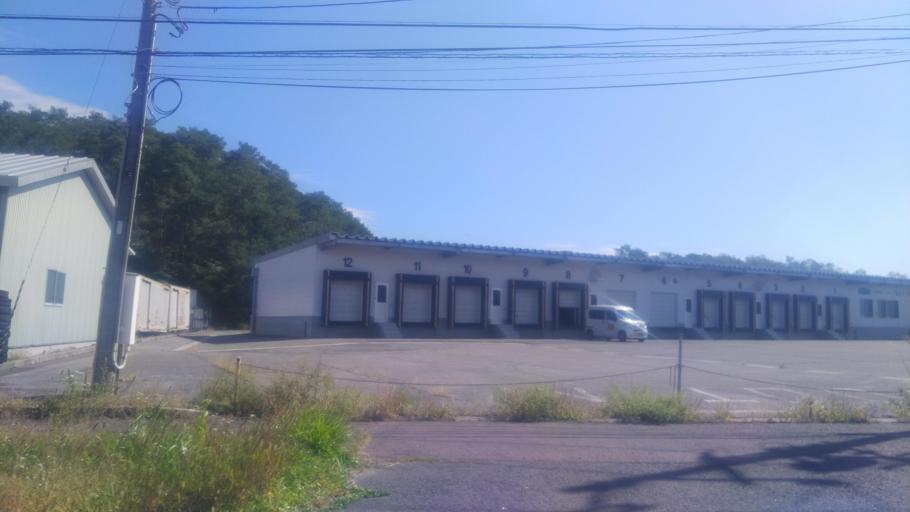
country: JP
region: Akita
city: Noshiromachi
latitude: 40.1891
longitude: 140.0141
